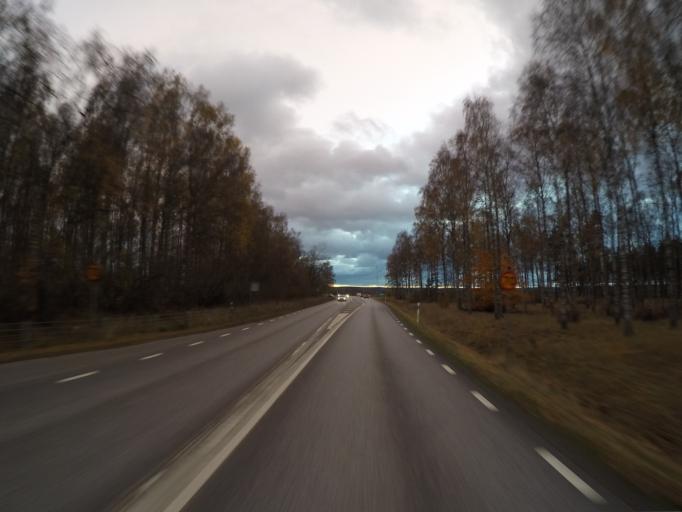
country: SE
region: Skane
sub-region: Kristianstads Kommun
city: Degeberga
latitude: 55.9037
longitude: 14.0720
